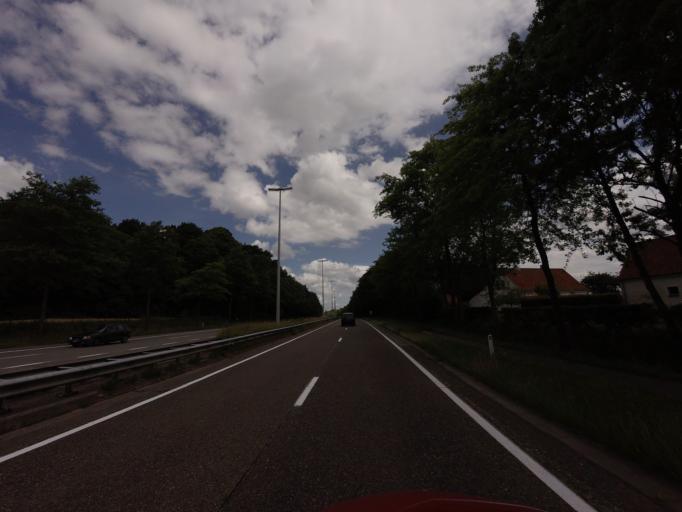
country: BE
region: Flanders
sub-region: Provincie Oost-Vlaanderen
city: Maldegem
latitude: 51.1713
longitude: 3.4458
